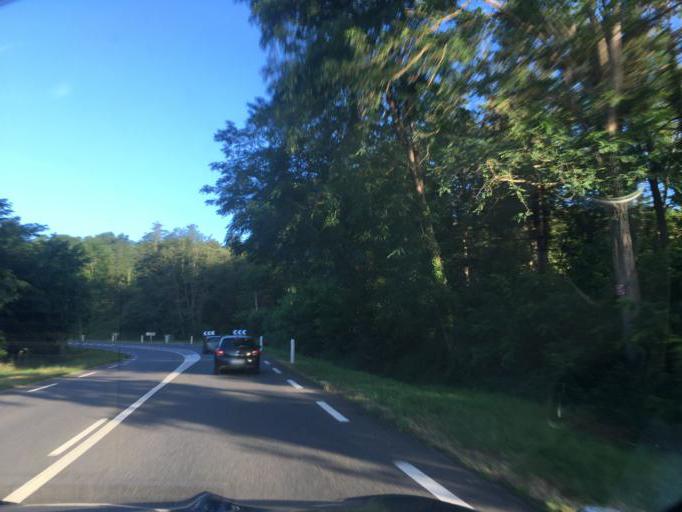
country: FR
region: Midi-Pyrenees
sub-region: Departement des Hautes-Pyrenees
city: Ibos
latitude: 43.2439
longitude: -0.0156
